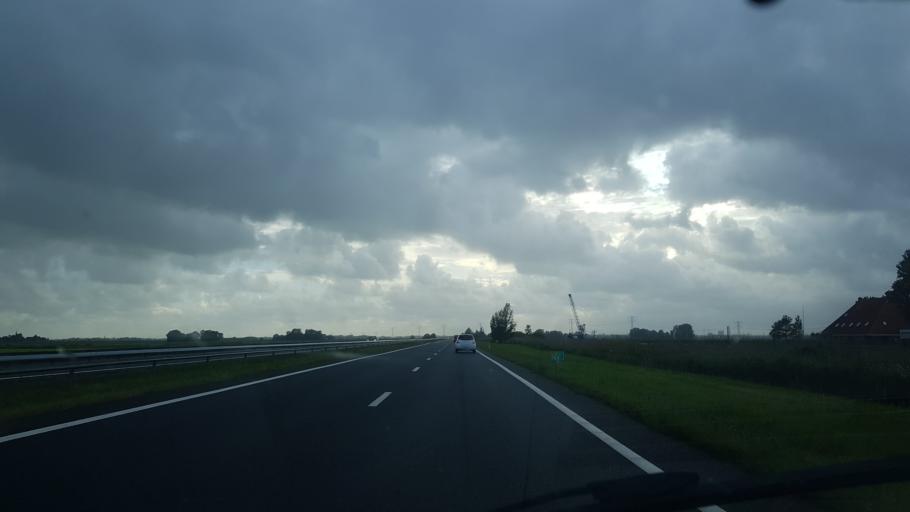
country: NL
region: Friesland
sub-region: Gemeente Boarnsterhim
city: Warten
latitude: 53.1694
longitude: 5.8905
